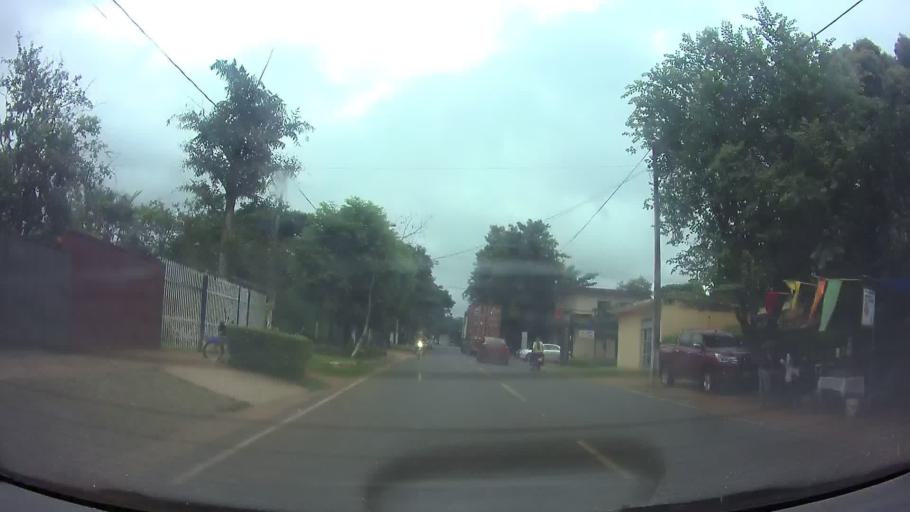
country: PY
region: Paraguari
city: Carapegua
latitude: -25.7665
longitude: -57.2478
